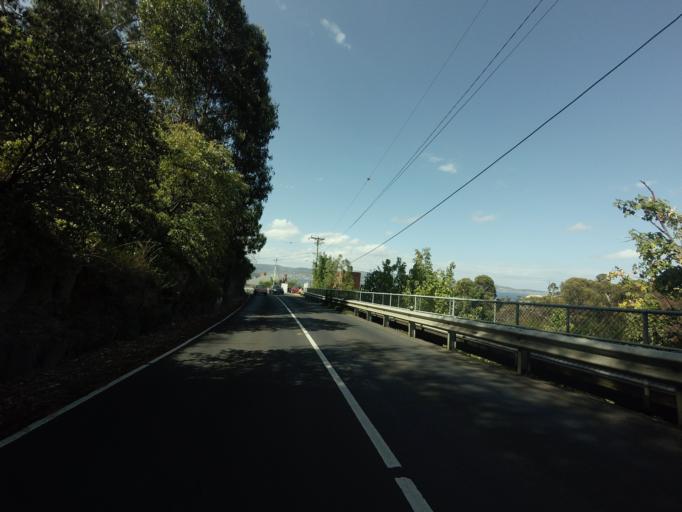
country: AU
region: Tasmania
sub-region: Hobart
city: Dynnyrne
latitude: -42.9040
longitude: 147.3189
